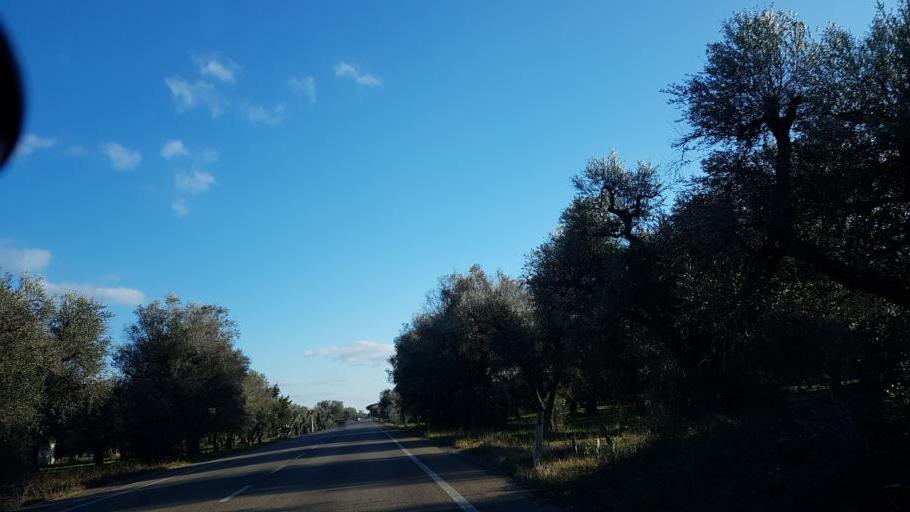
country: IT
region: Apulia
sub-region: Provincia di Lecce
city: Squinzano
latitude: 40.4579
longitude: 18.0228
